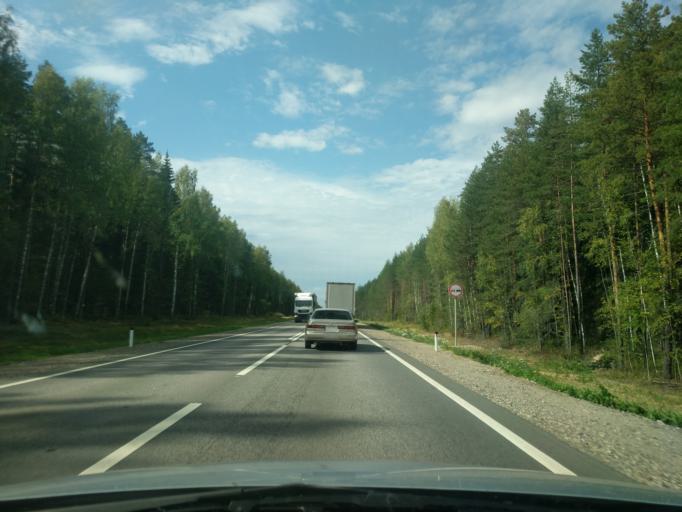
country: RU
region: Kostroma
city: Kadyy
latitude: 57.7971
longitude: 42.8403
